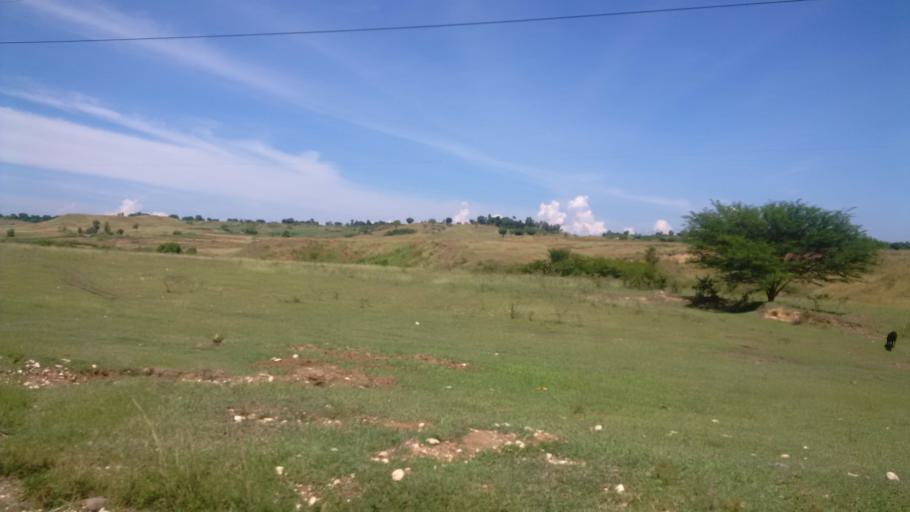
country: HT
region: Centre
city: Mayisad
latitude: 19.1488
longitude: -72.0903
